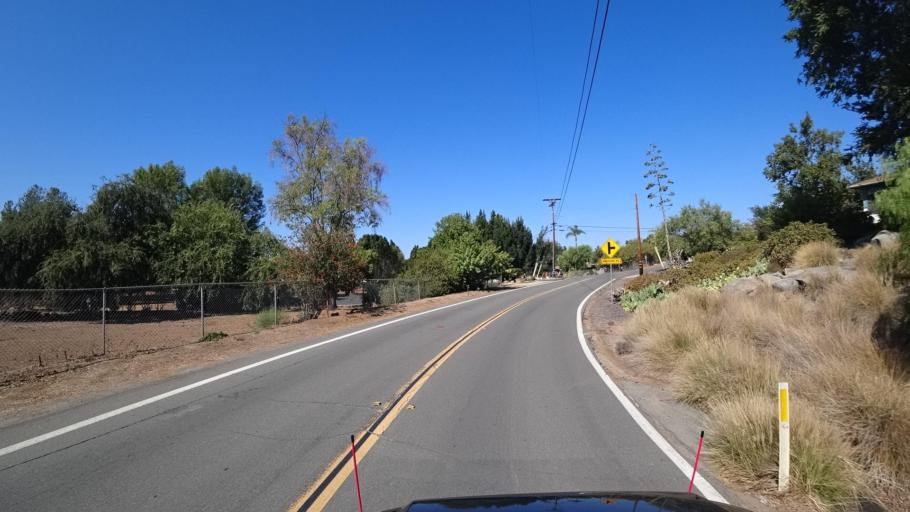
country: US
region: California
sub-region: San Diego County
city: Granite Hills
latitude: 32.7892
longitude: -116.9142
